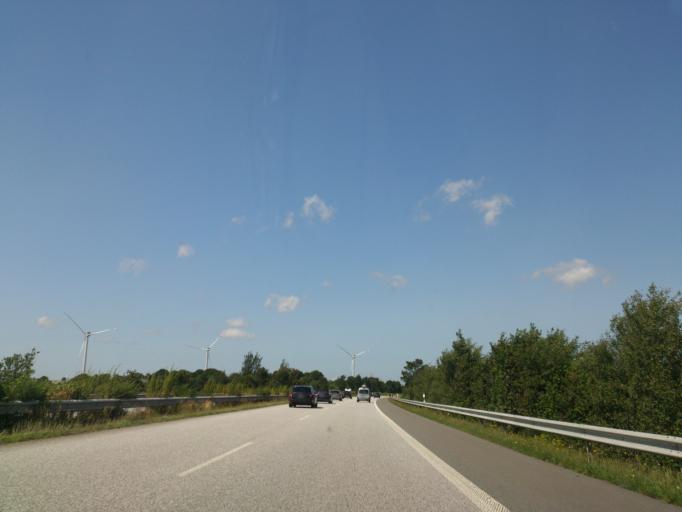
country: DE
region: Schleswig-Holstein
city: Hemmingstedt
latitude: 54.1725
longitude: 9.0698
